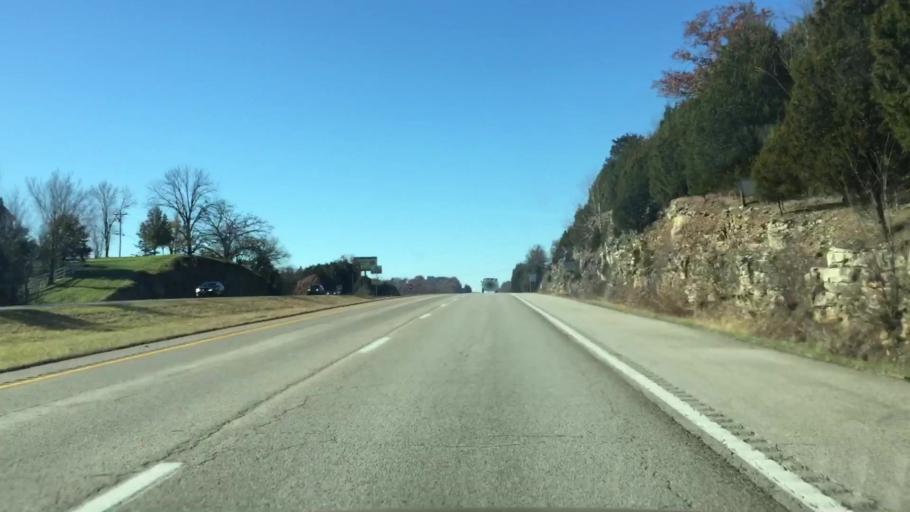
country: US
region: Missouri
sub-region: Cole County
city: Wardsville
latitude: 38.5250
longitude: -92.2258
